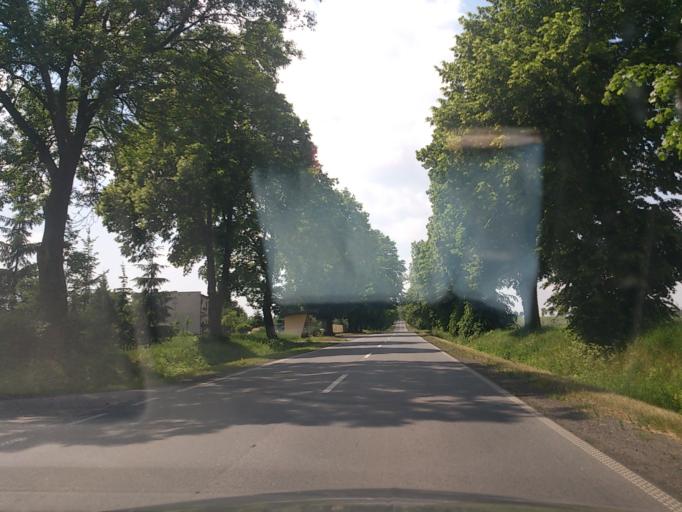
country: PL
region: Kujawsko-Pomorskie
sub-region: Powiat rypinski
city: Ostrowite
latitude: 53.0687
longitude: 19.3433
